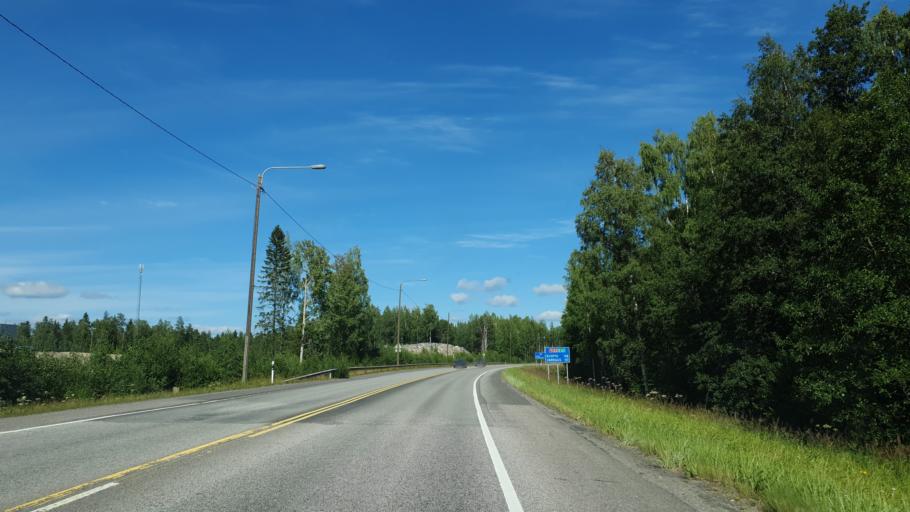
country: FI
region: Central Finland
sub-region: Jyvaeskylae
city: Saeynaetsalo
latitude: 62.2314
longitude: 25.9191
